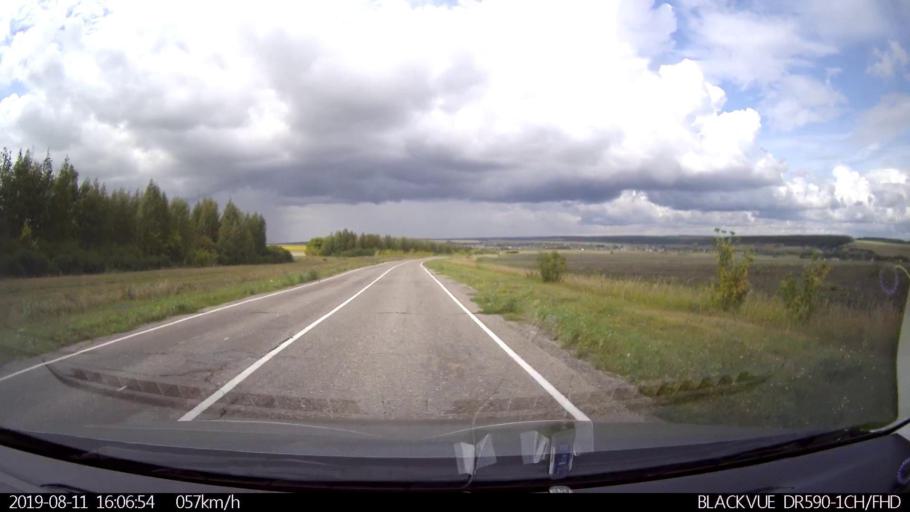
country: RU
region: Ulyanovsk
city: Ignatovka
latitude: 53.9723
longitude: 47.6457
